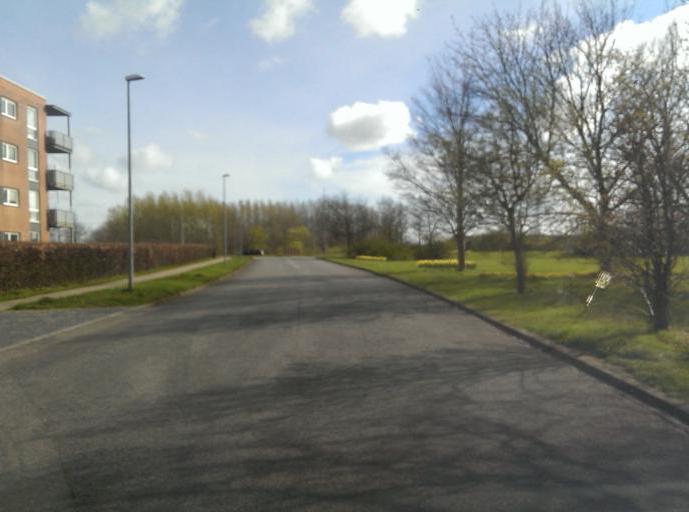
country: DK
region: South Denmark
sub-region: Esbjerg Kommune
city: Esbjerg
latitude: 55.4637
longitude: 8.4703
